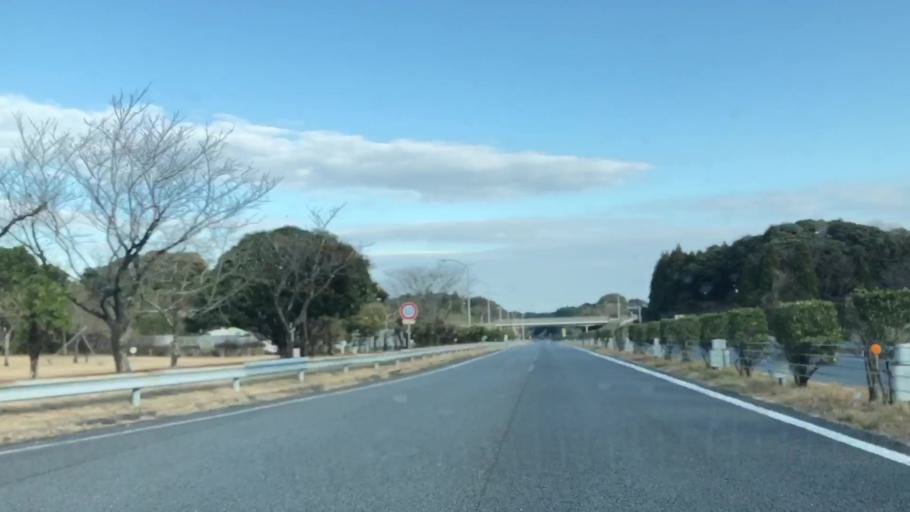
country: JP
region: Miyazaki
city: Miyazaki-shi
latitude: 31.8676
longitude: 131.4001
